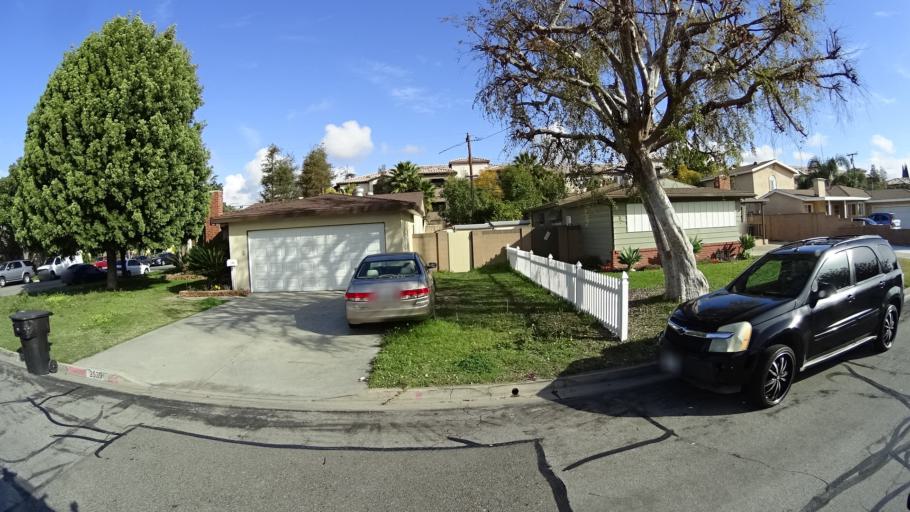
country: US
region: California
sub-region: Orange County
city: Stanton
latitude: 33.8235
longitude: -117.9737
